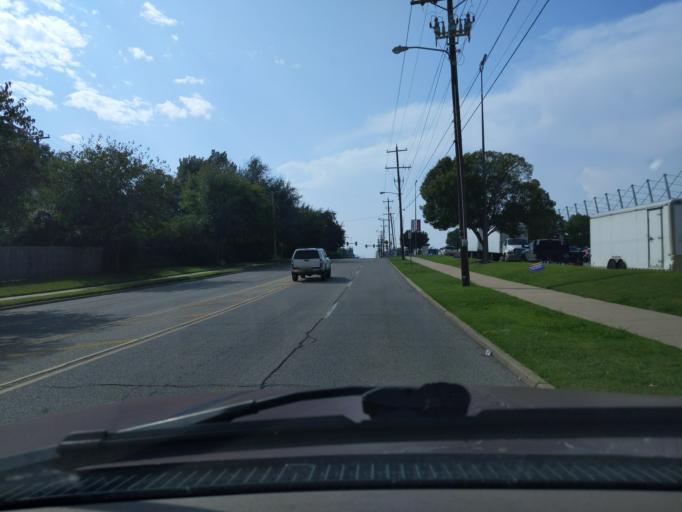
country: US
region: Oklahoma
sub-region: Tulsa County
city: Tulsa
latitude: 36.1333
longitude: -95.9293
